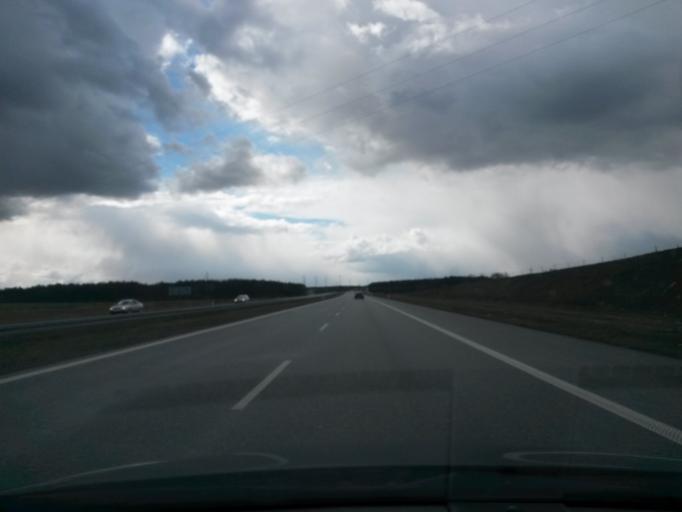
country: PL
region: Greater Poland Voivodeship
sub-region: Powiat koninski
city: Krzymow
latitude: 52.1419
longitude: 18.3773
